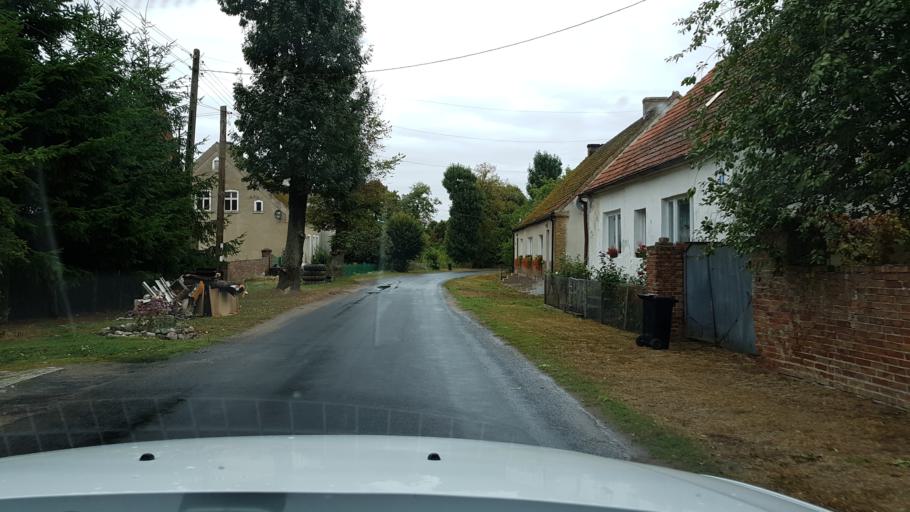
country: PL
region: West Pomeranian Voivodeship
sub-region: Powiat gryfinski
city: Cedynia
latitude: 52.8522
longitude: 14.2921
